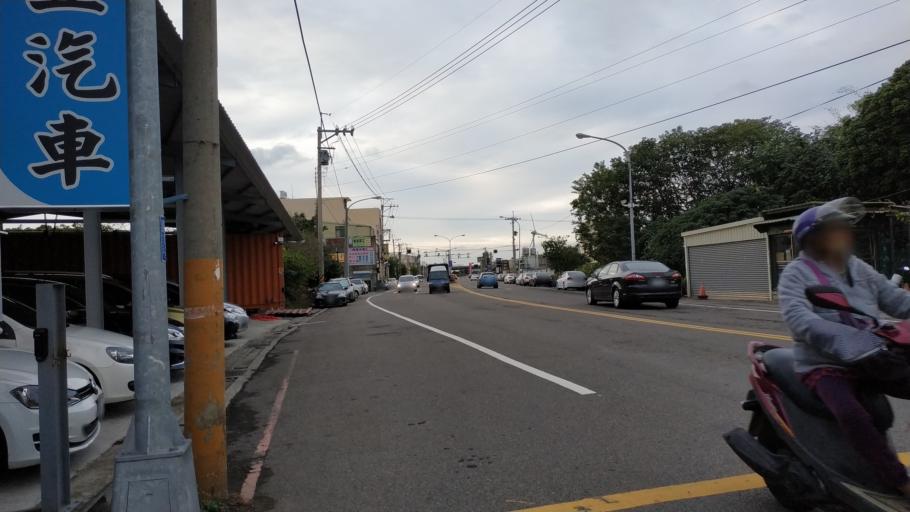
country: TW
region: Taiwan
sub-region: Miaoli
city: Miaoli
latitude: 24.6958
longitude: 120.8669
